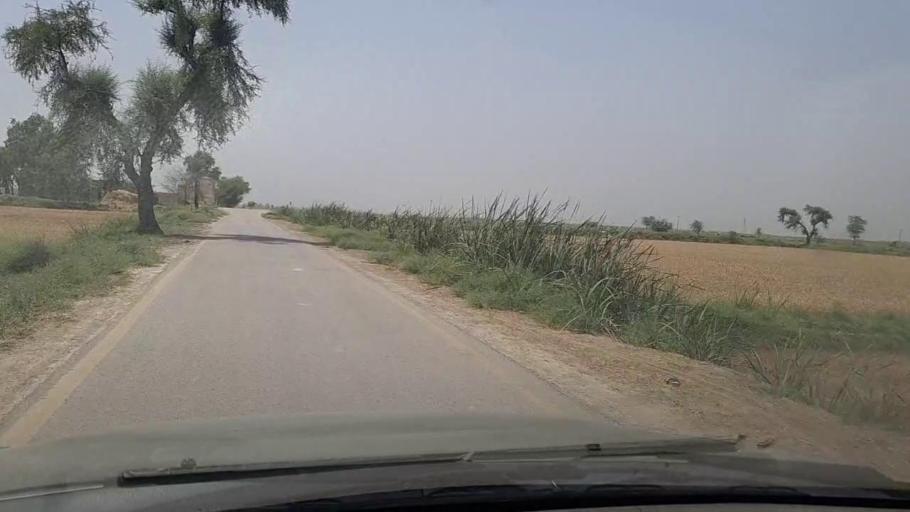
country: PK
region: Sindh
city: Miro Khan
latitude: 27.7716
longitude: 68.1561
